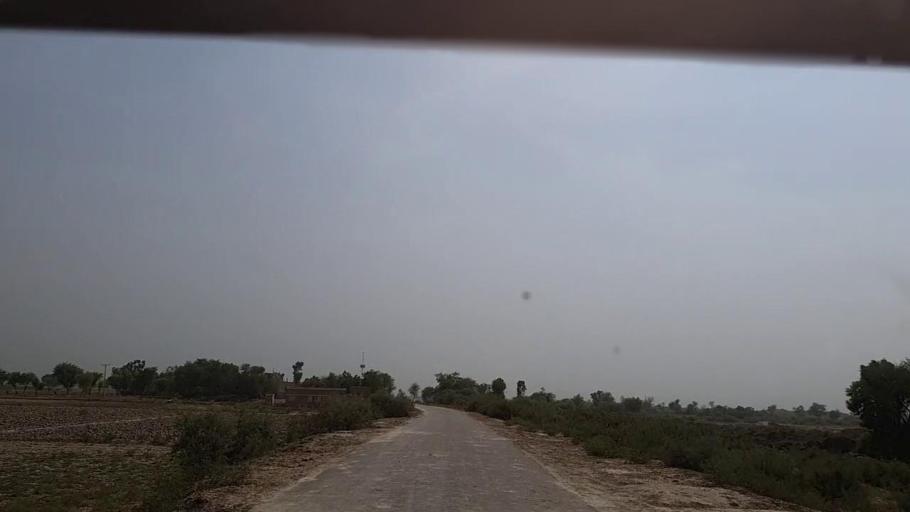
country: PK
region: Sindh
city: Khairpur Nathan Shah
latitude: 27.0353
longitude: 67.6830
